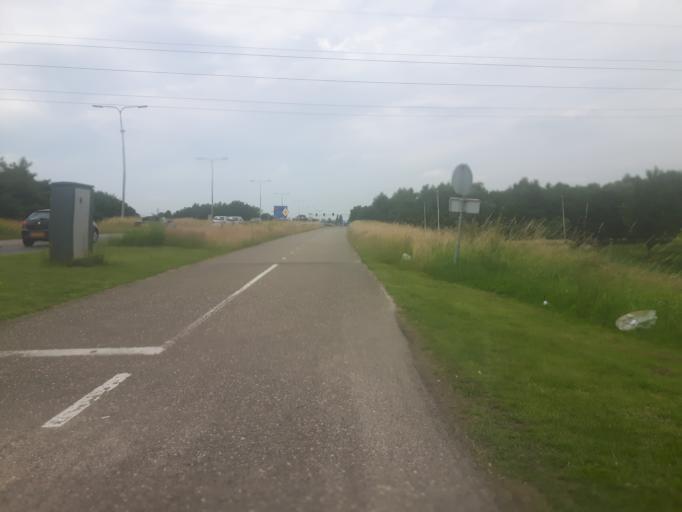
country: NL
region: Overijssel
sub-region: Gemeente Hengelo
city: Hengelo
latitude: 52.2863
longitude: 6.7731
